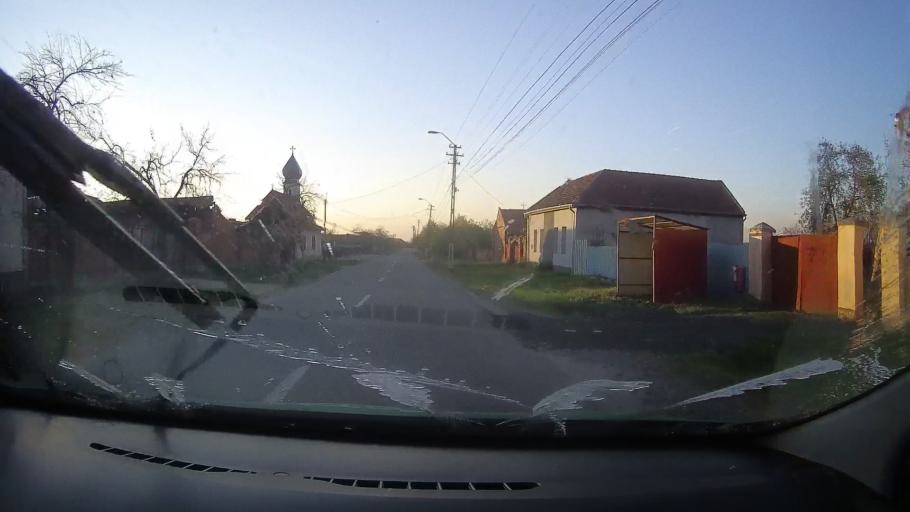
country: RO
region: Timis
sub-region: Comuna Traian Vuia
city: Traian Vuia
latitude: 45.7891
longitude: 22.0295
